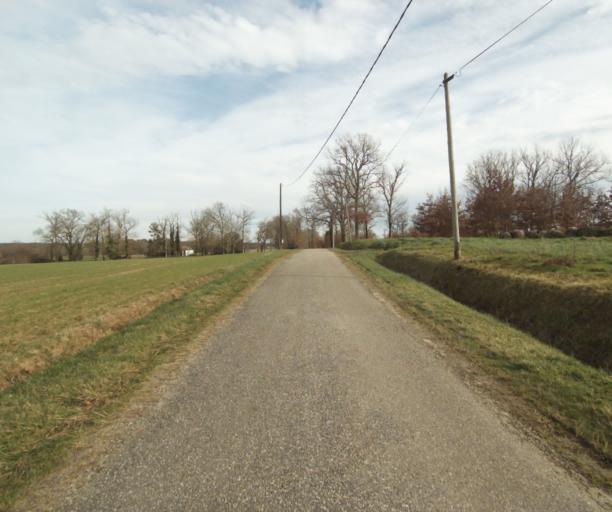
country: FR
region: Aquitaine
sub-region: Departement des Landes
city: Gabarret
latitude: 43.9730
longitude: 0.0329
